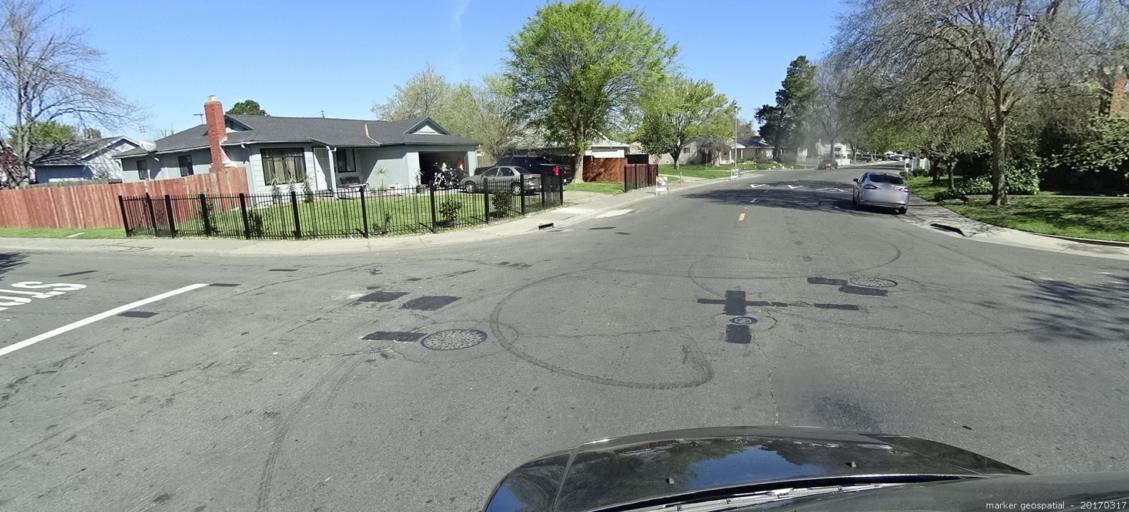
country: US
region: California
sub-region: Sacramento County
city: Parkway
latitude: 38.4822
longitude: -121.4933
